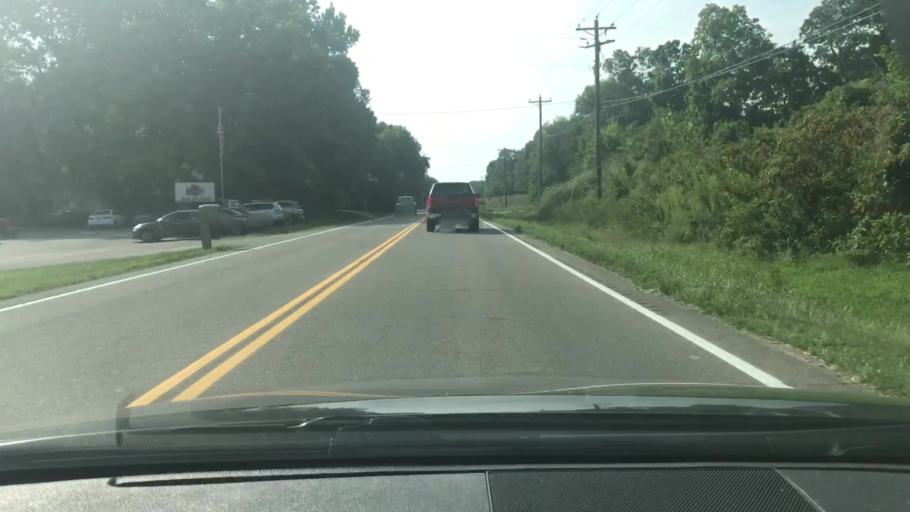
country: US
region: Tennessee
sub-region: Williamson County
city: Fairview
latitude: 36.0103
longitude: -87.1463
